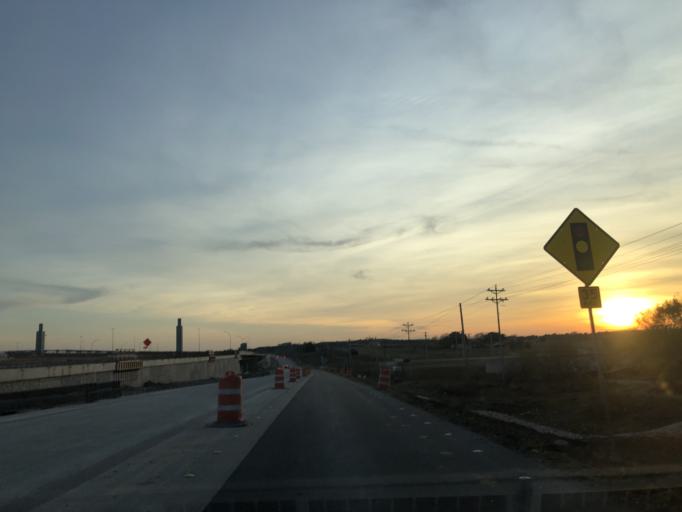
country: US
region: Texas
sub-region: Travis County
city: Manor
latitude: 30.3550
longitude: -97.5912
